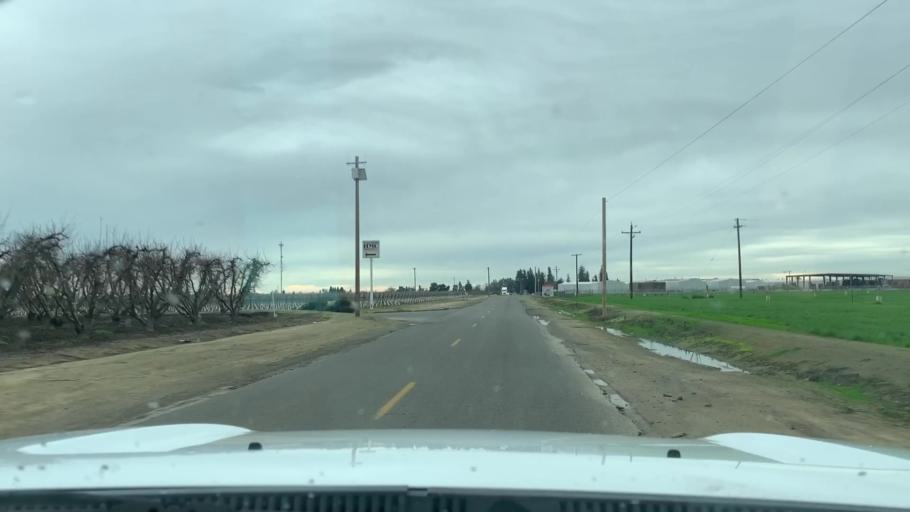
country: US
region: California
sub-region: Fresno County
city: Kingsburg
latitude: 36.5447
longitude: -119.5752
